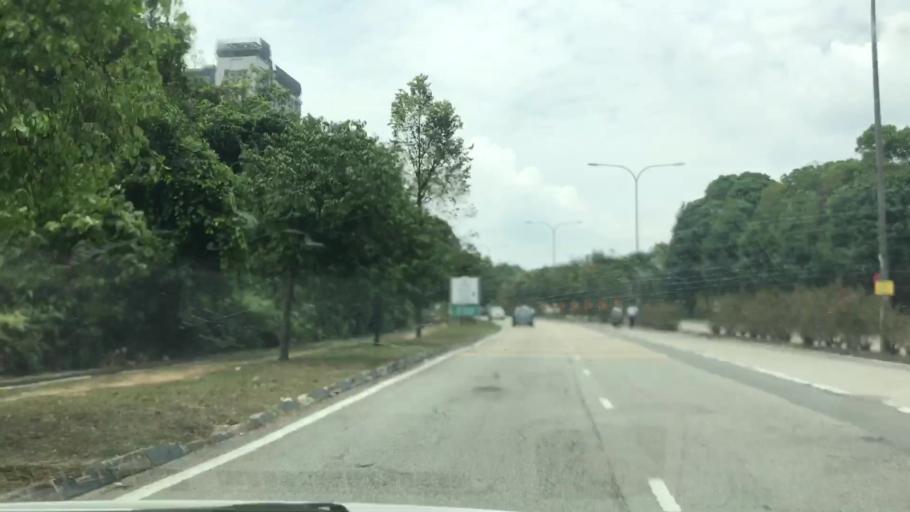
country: MY
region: Selangor
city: Kampong Baharu Balakong
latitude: 3.0536
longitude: 101.6769
